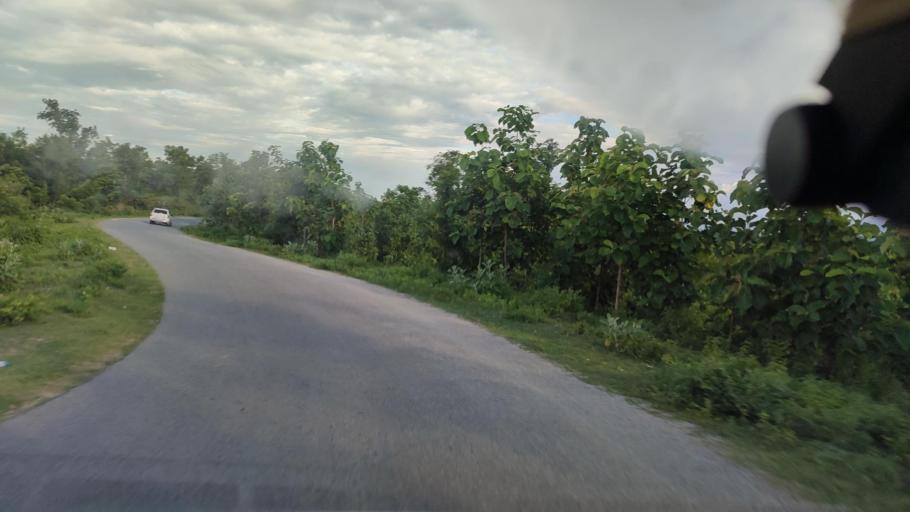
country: MM
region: Magway
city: Taungdwingyi
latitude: 20.0172
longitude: 95.8281
